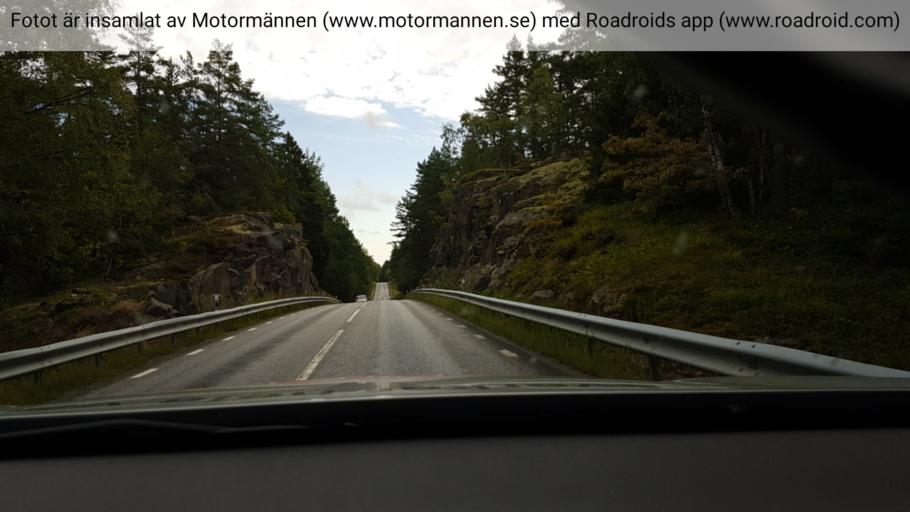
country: SE
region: Stockholm
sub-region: Vaxholms Kommun
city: Resaro
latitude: 59.5387
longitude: 18.4600
